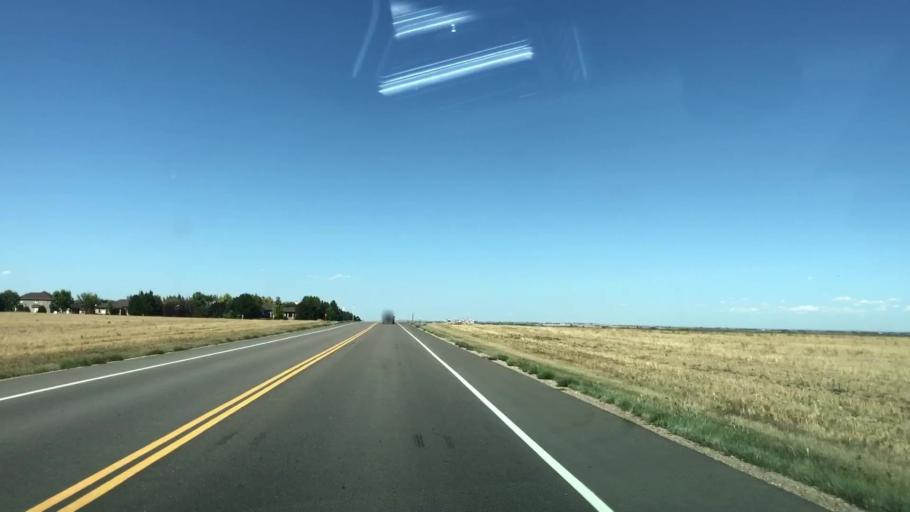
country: US
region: Colorado
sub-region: Weld County
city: Windsor
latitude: 40.4584
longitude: -104.9441
